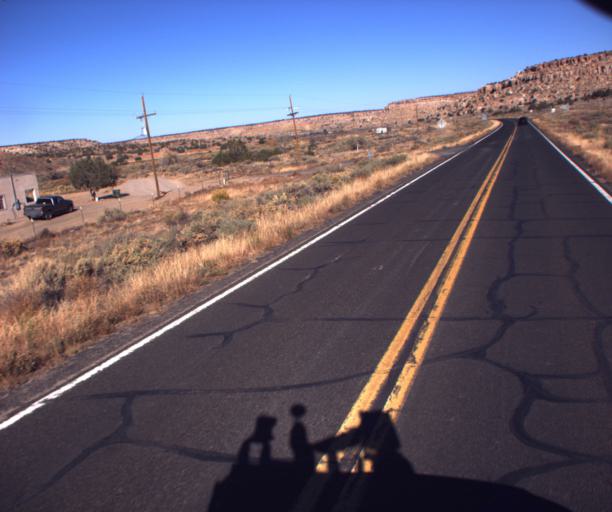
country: US
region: Arizona
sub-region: Navajo County
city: First Mesa
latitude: 35.8254
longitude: -110.2207
